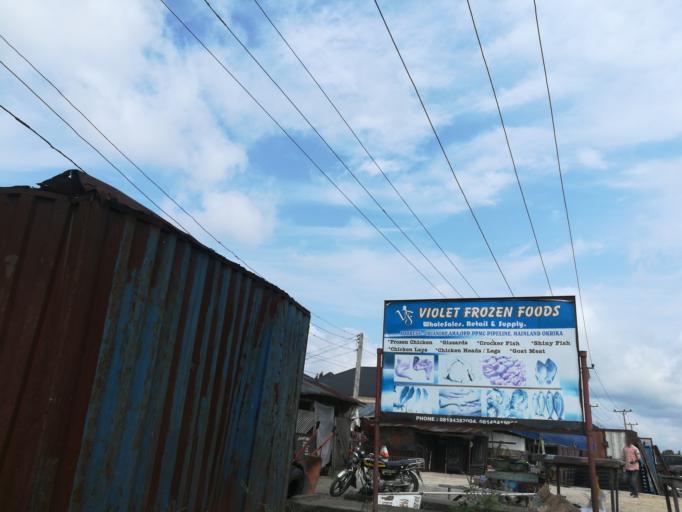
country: NG
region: Rivers
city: Okrika
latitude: 4.7595
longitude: 7.0976
